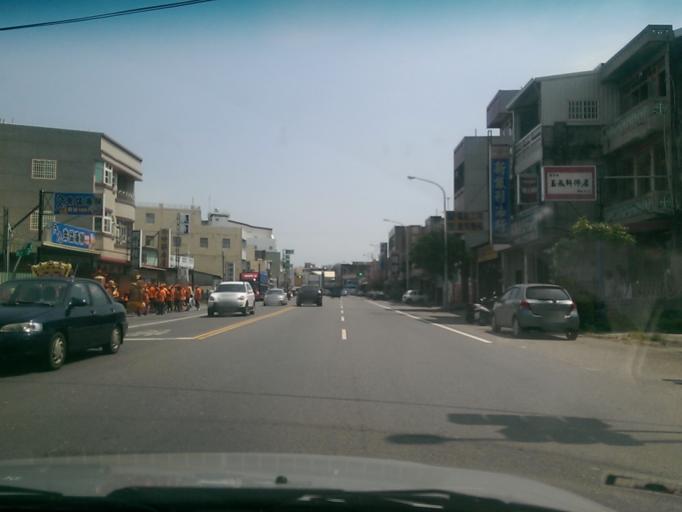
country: TW
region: Taiwan
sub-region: Chiayi
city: Taibao
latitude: 23.5805
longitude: 120.2984
